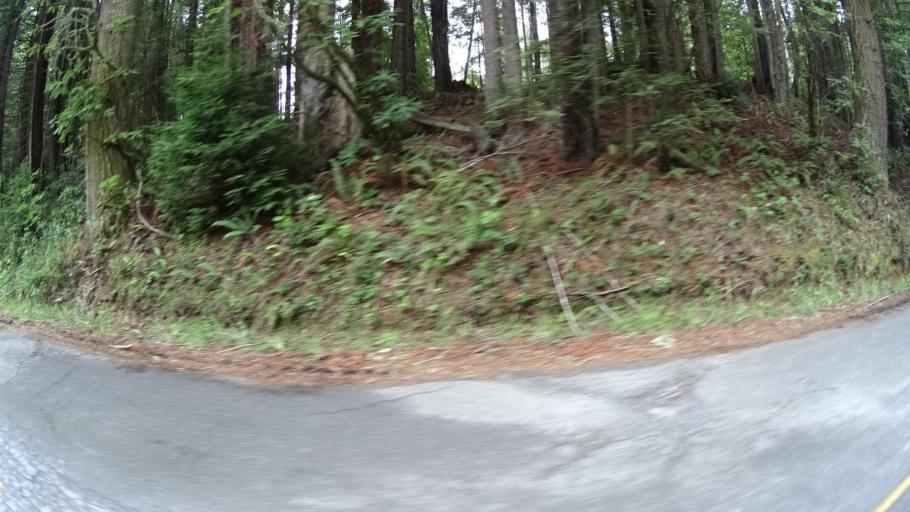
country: US
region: California
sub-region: Humboldt County
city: Bayside
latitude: 40.7999
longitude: -124.0380
